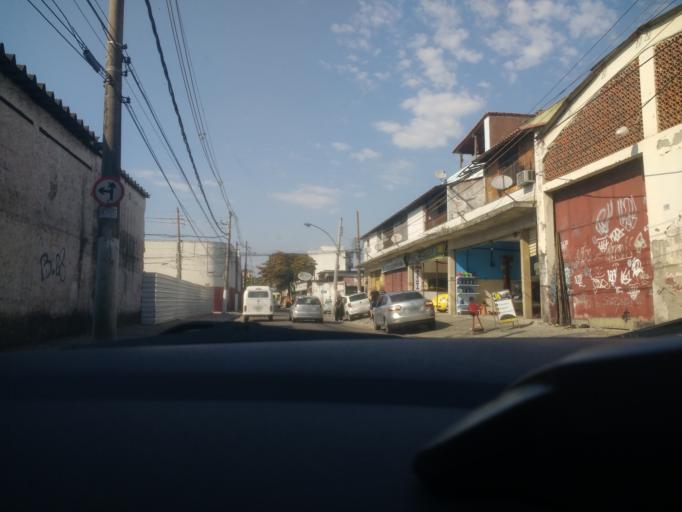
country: BR
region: Rio de Janeiro
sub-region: Duque De Caxias
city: Duque de Caxias
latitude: -22.7967
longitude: -43.2958
